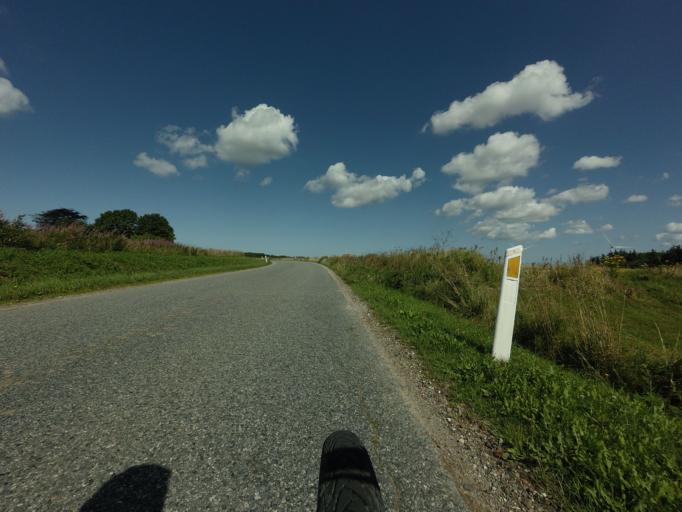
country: DK
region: North Denmark
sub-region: Hjorring Kommune
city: Hjorring
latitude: 57.4842
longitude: 9.9010
